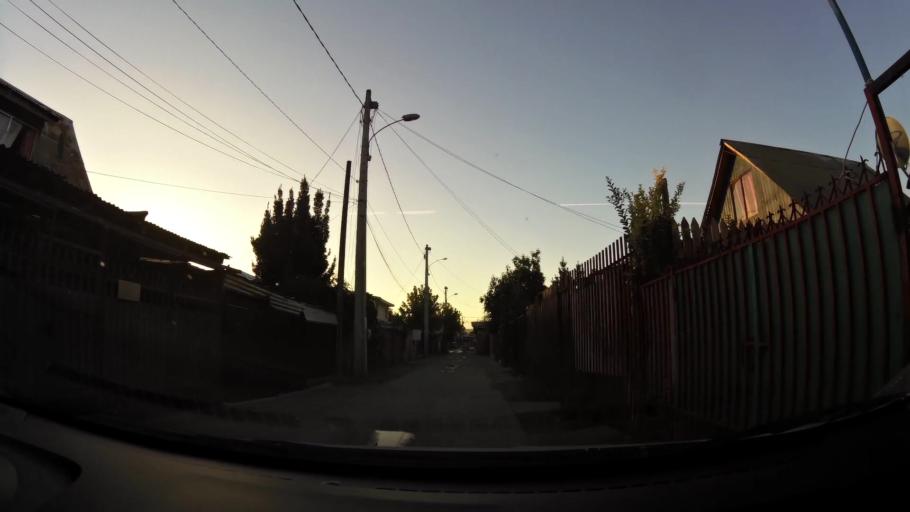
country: CL
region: Maule
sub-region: Provincia de Talca
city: Talca
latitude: -35.4473
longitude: -71.6366
